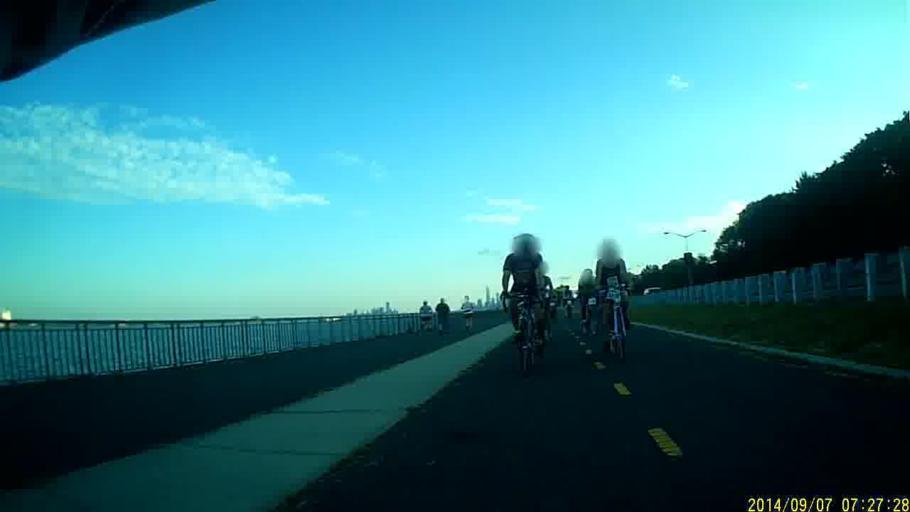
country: US
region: New York
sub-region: Kings County
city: Bensonhurst
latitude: 40.6354
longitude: -74.0384
